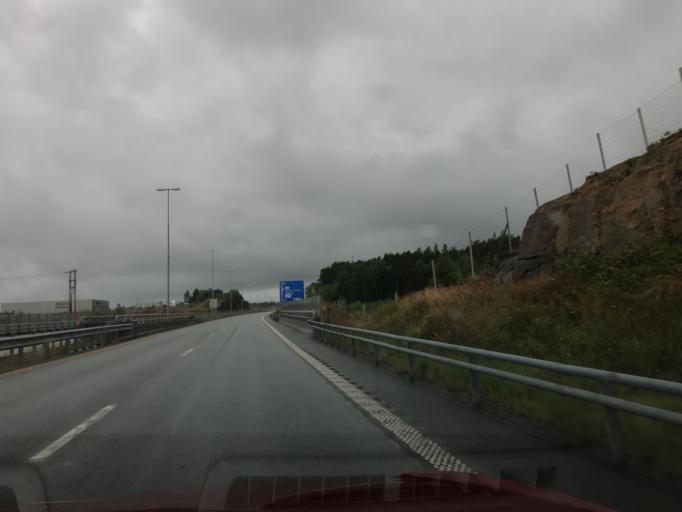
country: NO
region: Aust-Agder
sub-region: Lillesand
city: Lillesand
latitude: 58.2751
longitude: 8.4057
